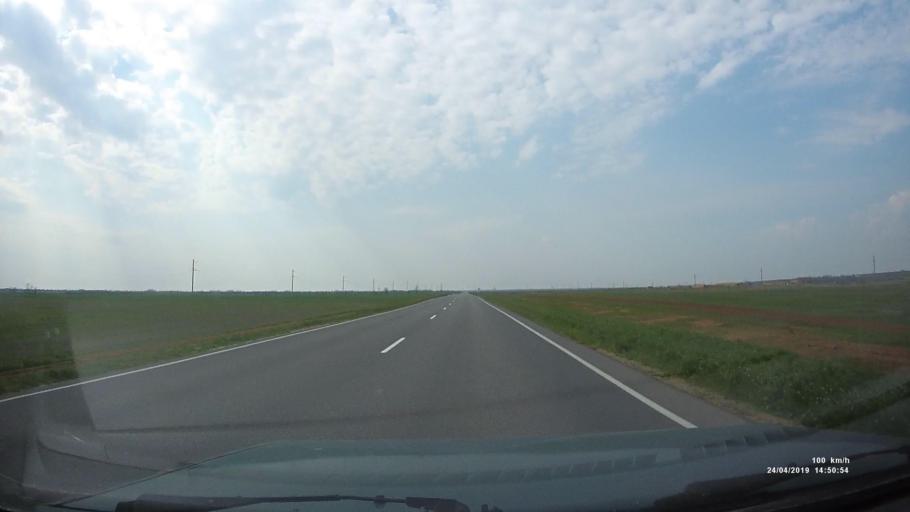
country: RU
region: Rostov
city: Remontnoye
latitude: 46.5209
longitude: 43.7108
